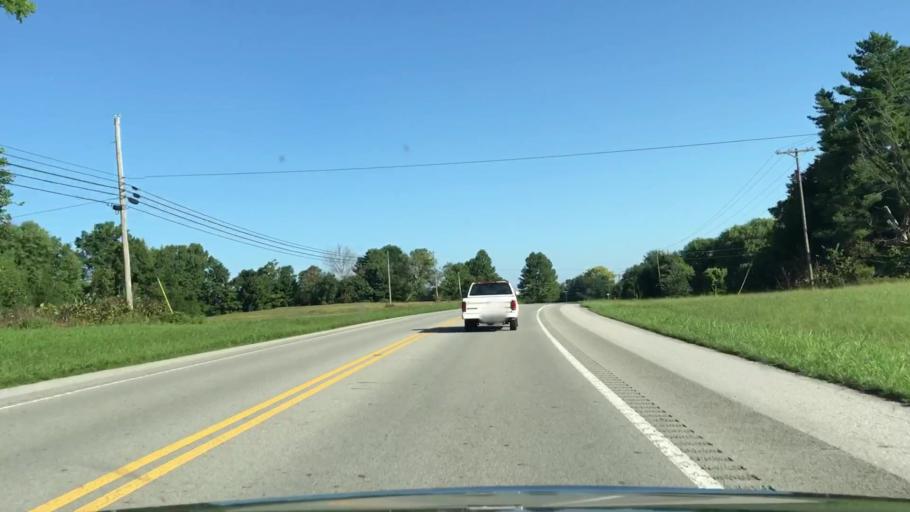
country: US
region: Tennessee
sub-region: Jackson County
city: Gainesboro
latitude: 36.2861
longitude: -85.6304
